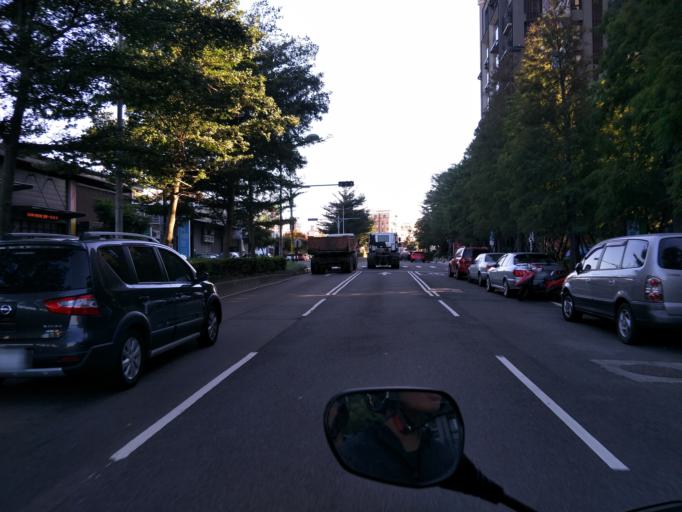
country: TW
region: Taiwan
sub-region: Hsinchu
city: Zhubei
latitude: 24.8390
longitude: 121.0210
